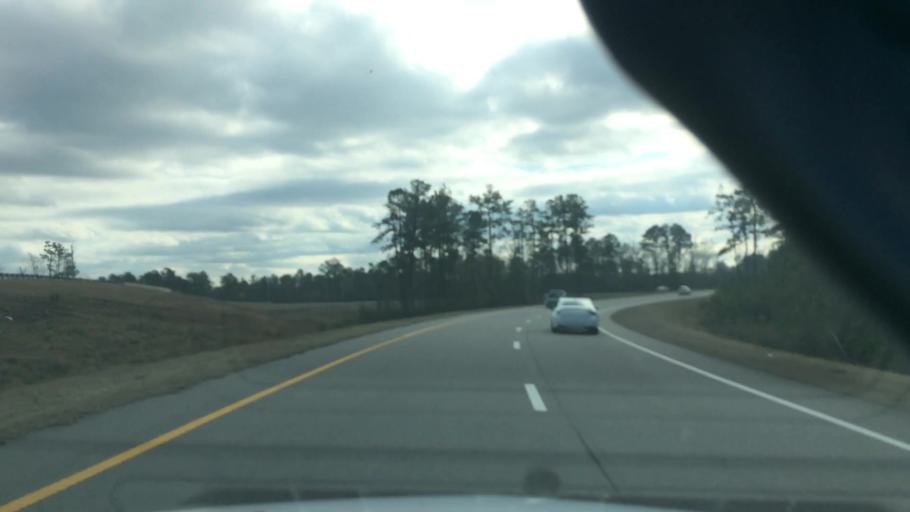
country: US
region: North Carolina
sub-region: Brunswick County
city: Leland
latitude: 34.1920
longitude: -78.0796
